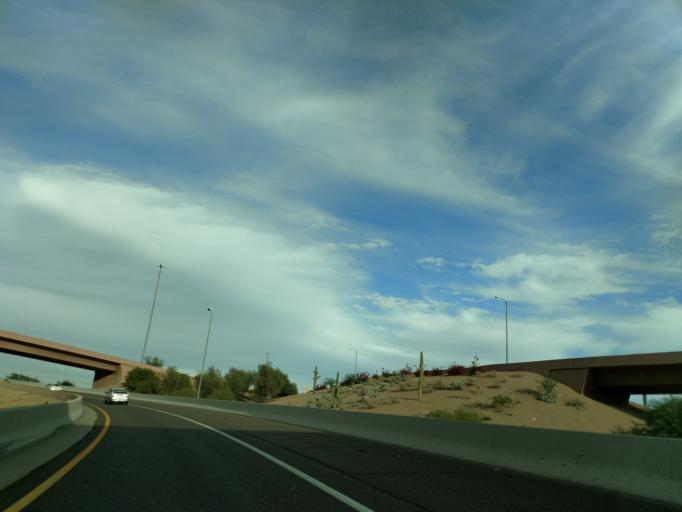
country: US
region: Arizona
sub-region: Maricopa County
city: Tempe
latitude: 33.4322
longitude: -111.8900
